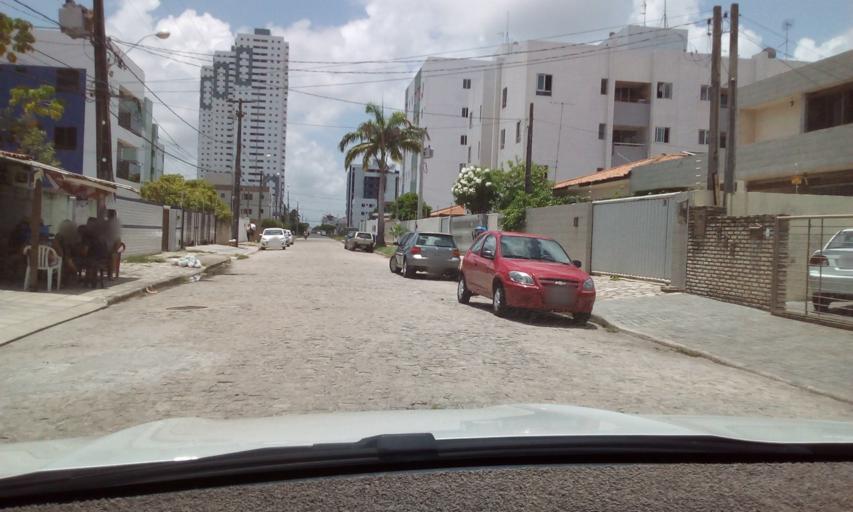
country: BR
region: Paraiba
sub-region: Joao Pessoa
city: Joao Pessoa
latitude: -7.0720
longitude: -34.8377
